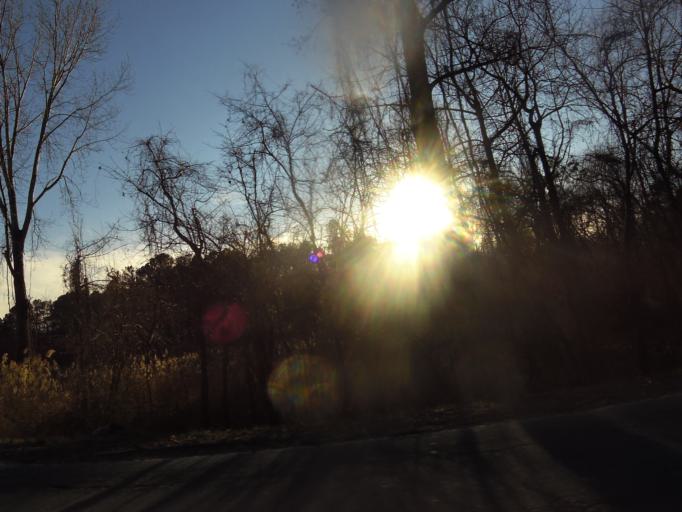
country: US
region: Virginia
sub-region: City of Franklin
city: Franklin
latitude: 36.6754
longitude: -76.9005
